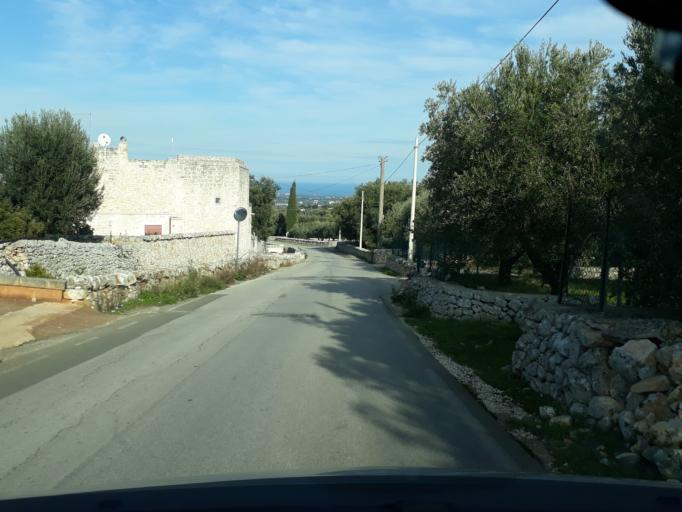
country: IT
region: Apulia
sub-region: Provincia di Brindisi
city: Lamie di Olimpie-Selva
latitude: 40.8081
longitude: 17.3538
